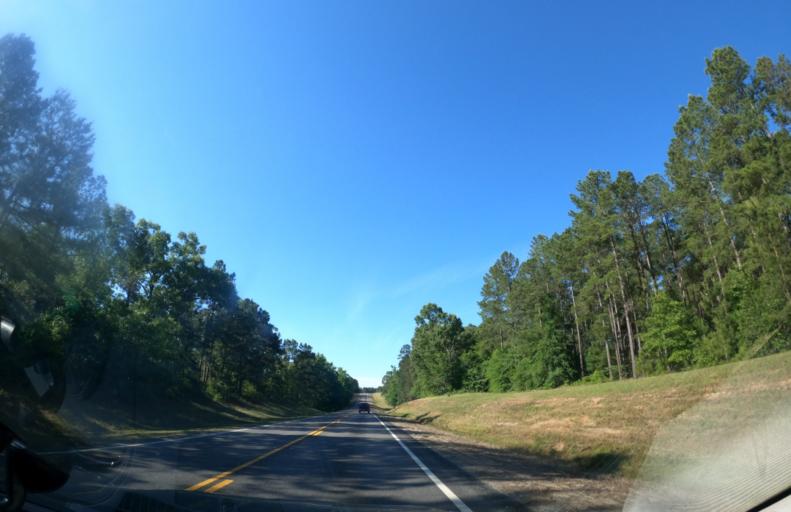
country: US
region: Georgia
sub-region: Columbia County
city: Harlem
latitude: 33.3622
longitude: -82.3248
